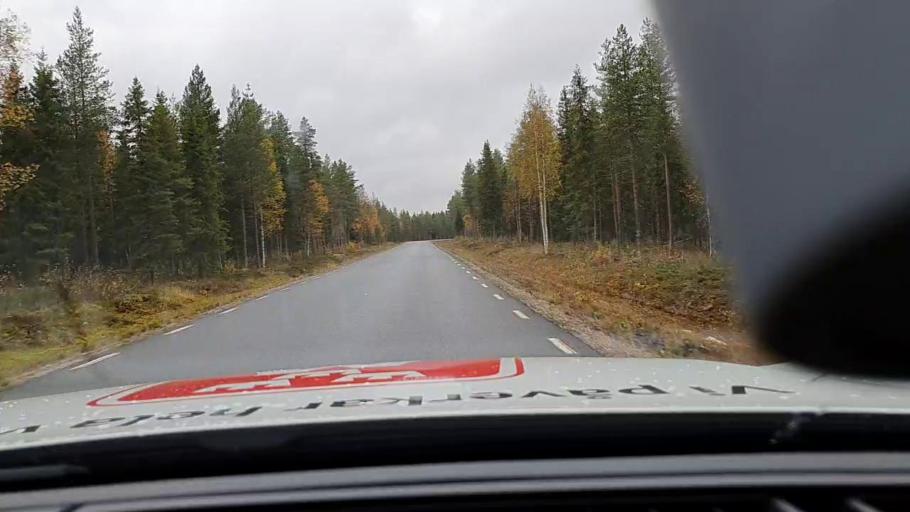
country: SE
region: Norrbotten
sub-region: Haparanda Kommun
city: Haparanda
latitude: 65.9376
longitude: 23.8072
